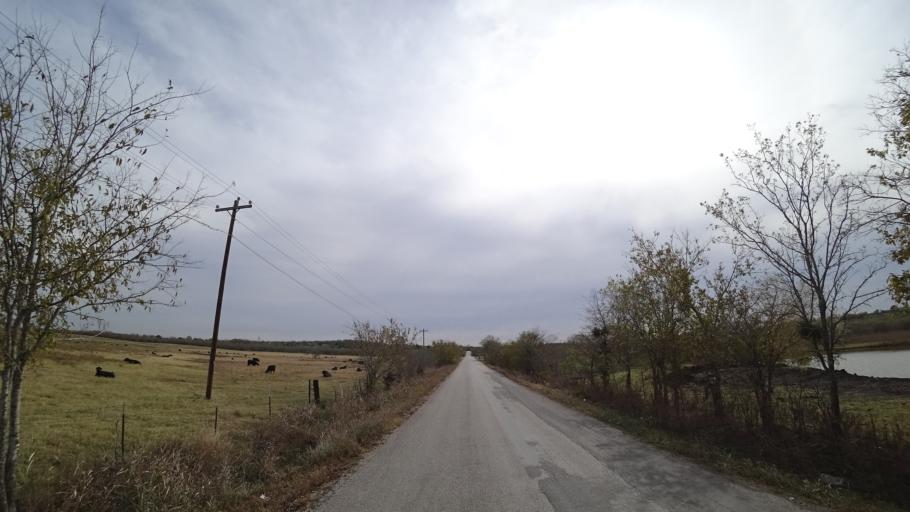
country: US
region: Texas
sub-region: Travis County
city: Garfield
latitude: 30.1171
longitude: -97.5910
